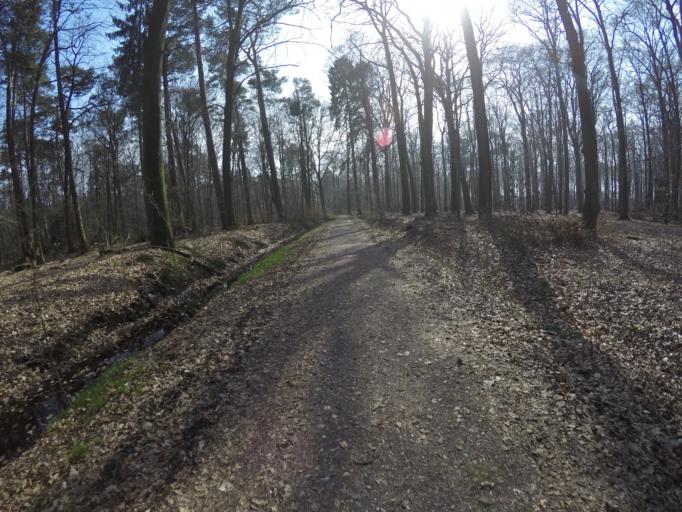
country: DE
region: Schleswig-Holstein
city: Ellerhoop
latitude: 53.7195
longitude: 9.7938
